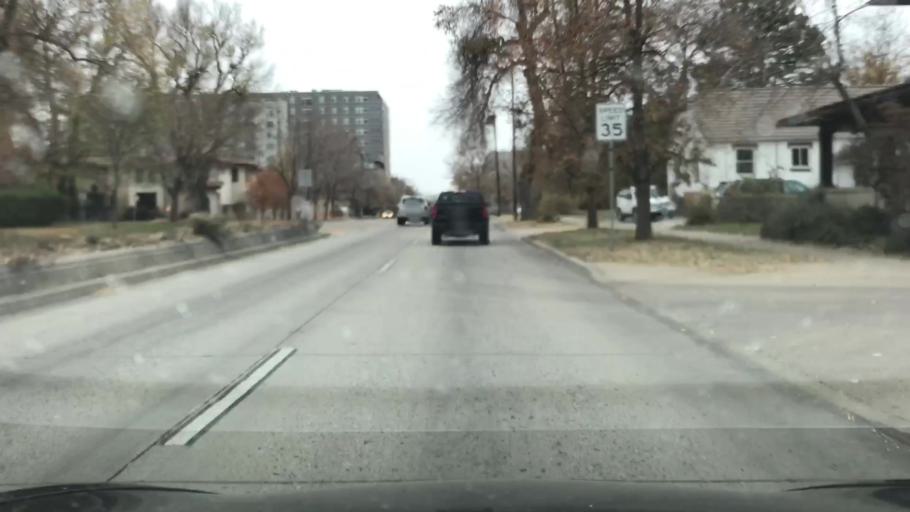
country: US
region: Colorado
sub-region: Arapahoe County
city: Glendale
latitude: 39.6785
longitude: -104.9558
